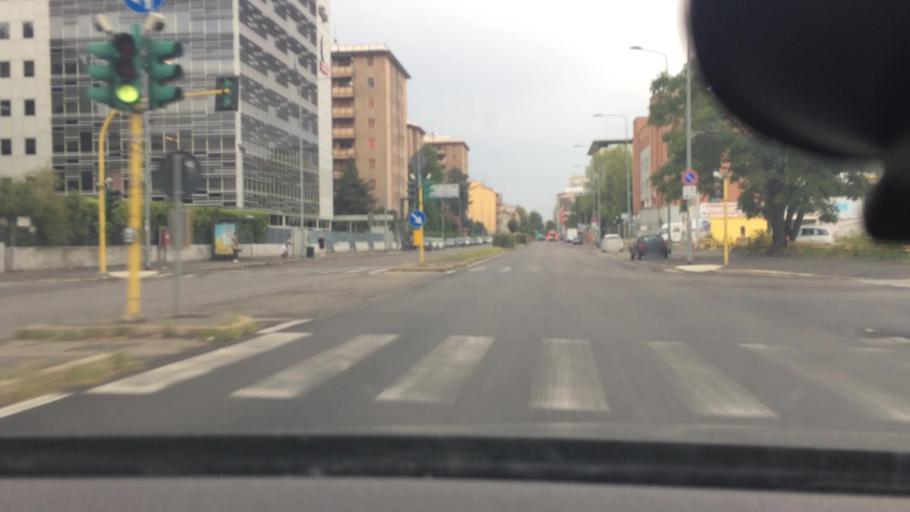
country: IT
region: Lombardy
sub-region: Citta metropolitana di Milano
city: Sesto San Giovanni
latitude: 45.5202
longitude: 9.2270
